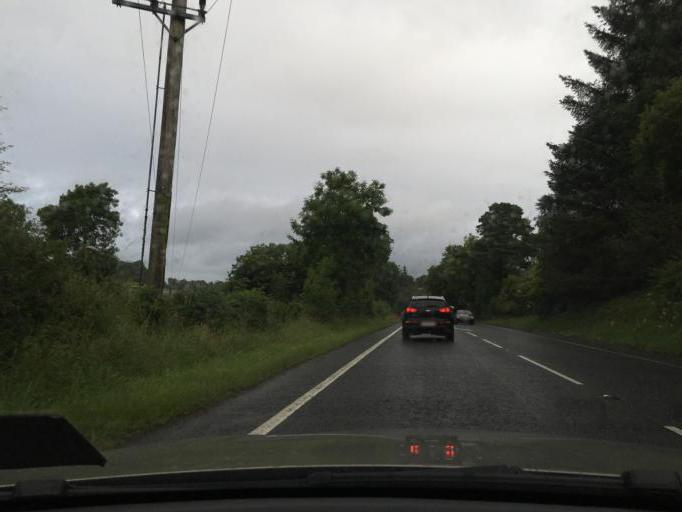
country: GB
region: Northern Ireland
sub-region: Fermanagh District
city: Enniskillen
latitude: 54.3815
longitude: -7.6369
